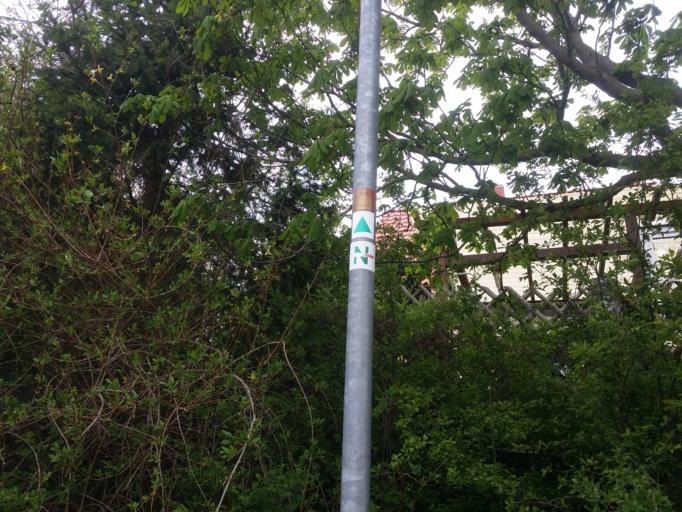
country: DE
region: Saxony-Anhalt
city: Neinstedt
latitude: 51.7434
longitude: 11.0862
